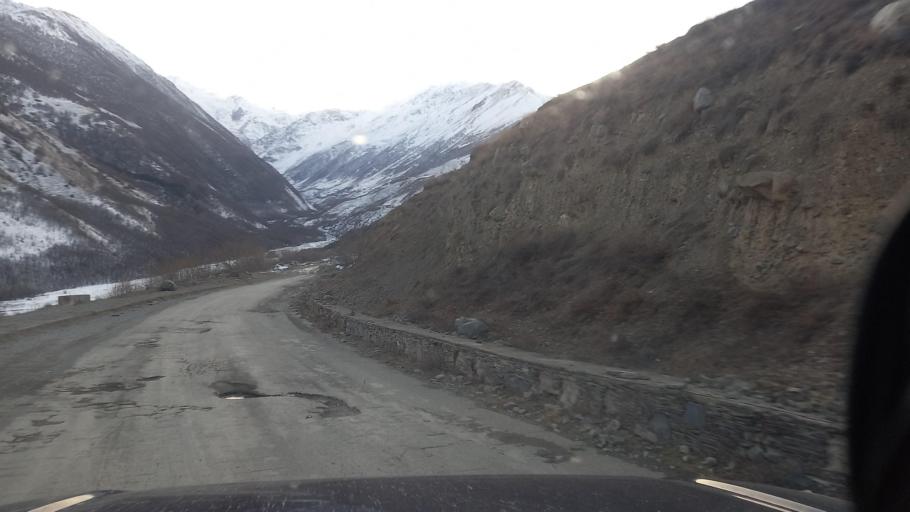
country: RU
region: Ingushetiya
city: Dzhayrakh
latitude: 42.8409
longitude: 44.5125
